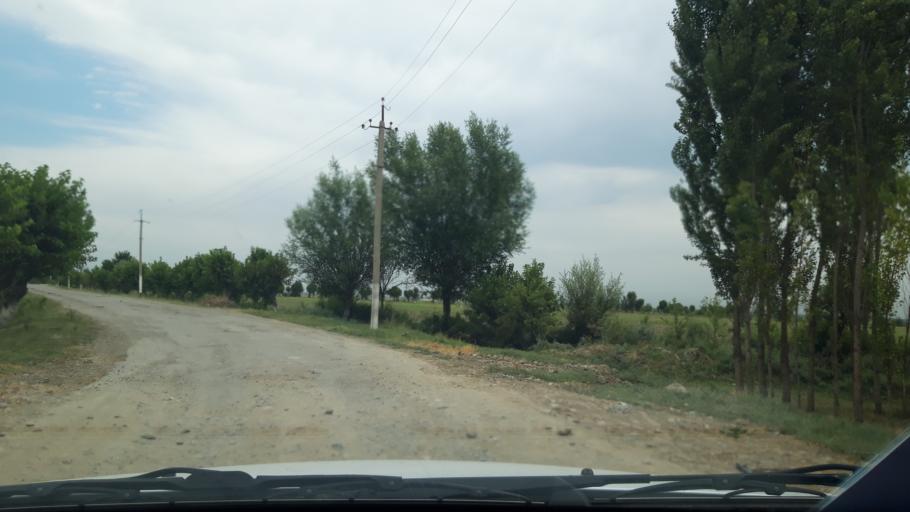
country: UZ
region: Namangan
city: Uychi
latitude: 41.0181
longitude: 71.9199
